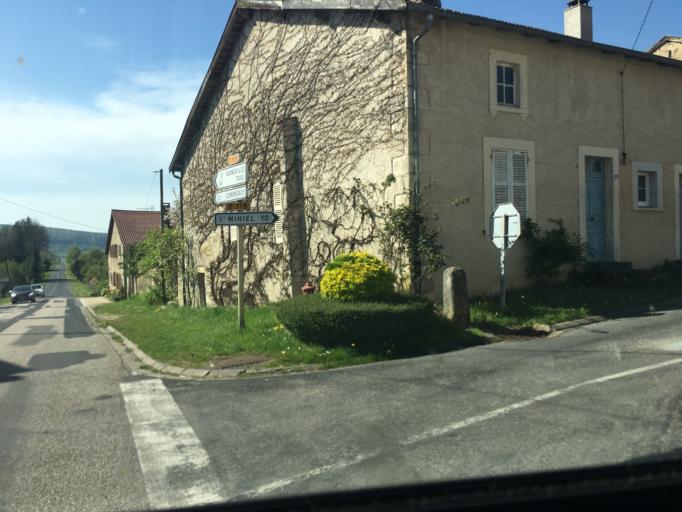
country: FR
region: Lorraine
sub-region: Departement de la Meuse
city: Vigneulles-les-Hattonchatel
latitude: 48.8966
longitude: 5.6594
